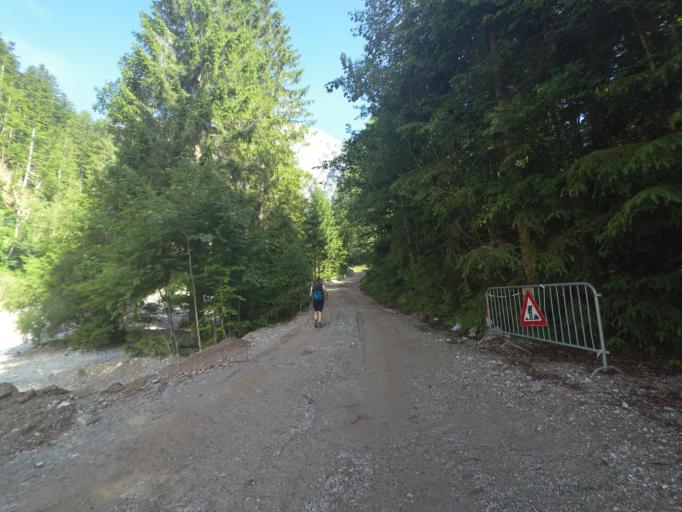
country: AT
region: Salzburg
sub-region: Politischer Bezirk Zell am See
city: Leogang
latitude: 47.4540
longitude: 12.7543
